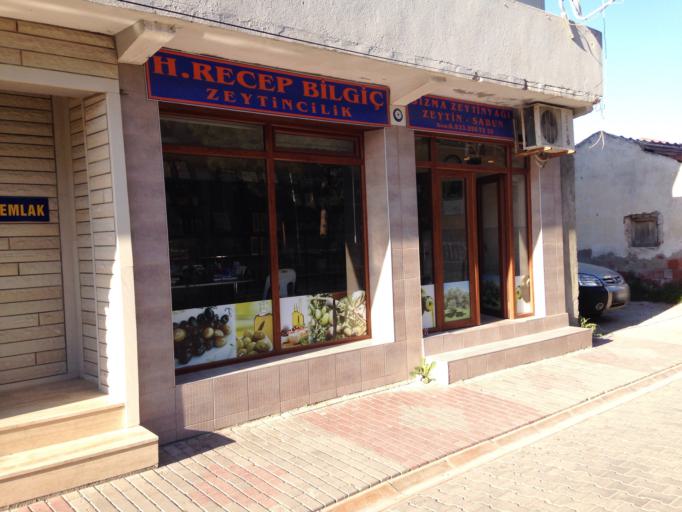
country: TR
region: Canakkale
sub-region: Merkez
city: Kucukkuyu
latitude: 39.5464
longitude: 26.6025
